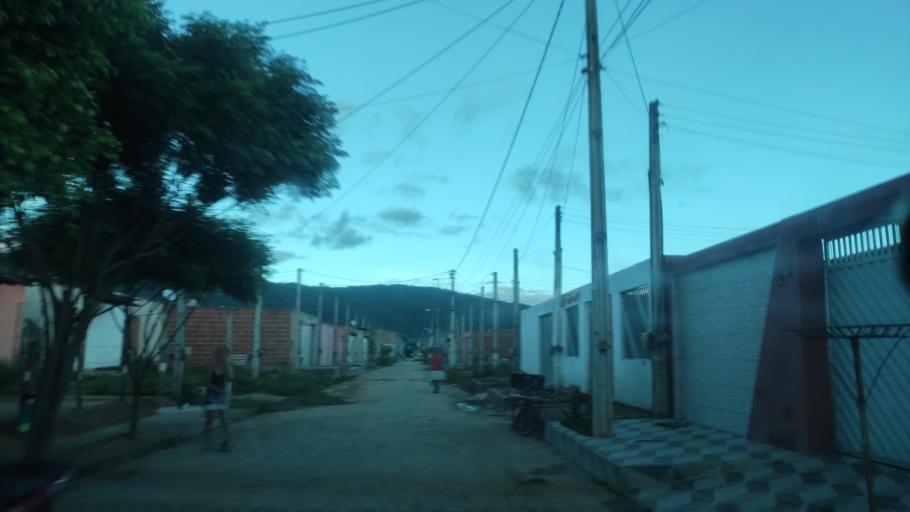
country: BR
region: Alagoas
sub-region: Uniao Dos Palmares
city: Uniao dos Palmares
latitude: -9.1458
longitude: -36.0034
